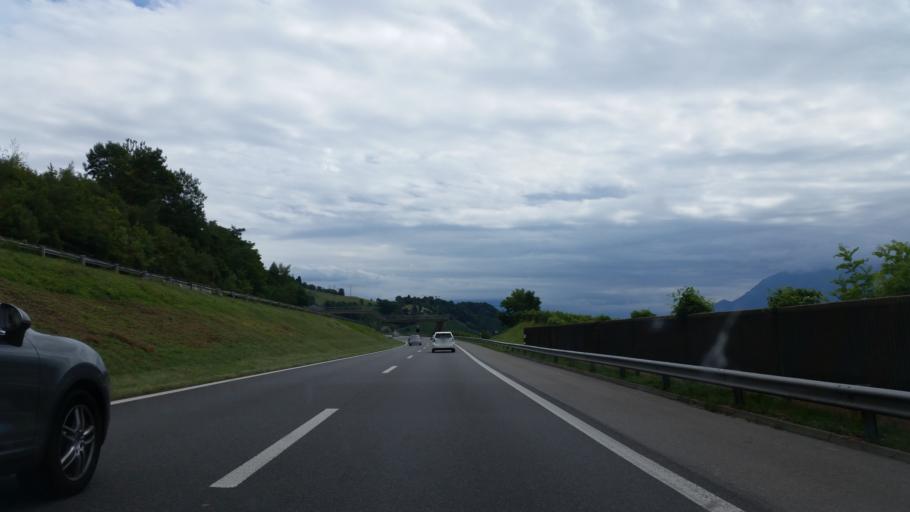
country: CH
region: Vaud
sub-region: Lavaux-Oron District
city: Cully
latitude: 46.4991
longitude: 6.7378
